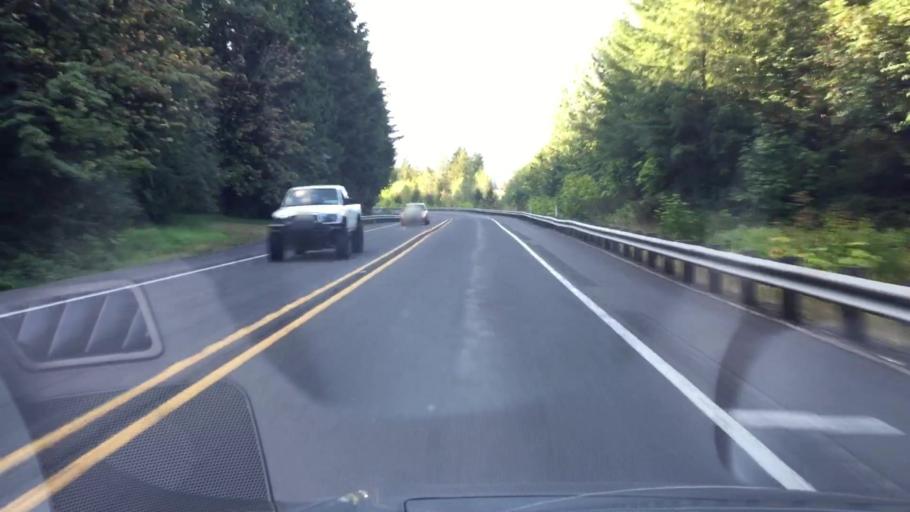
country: US
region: Washington
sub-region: Lewis County
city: Morton
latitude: 46.5193
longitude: -122.2183
